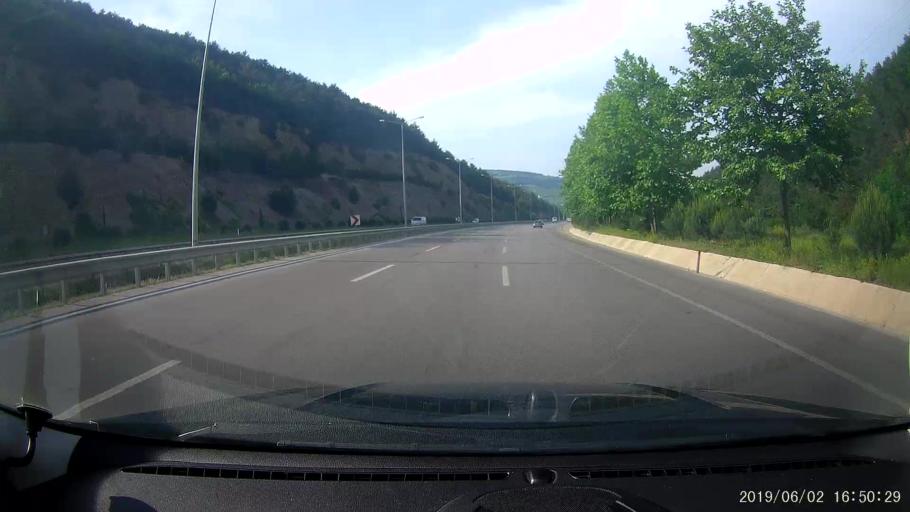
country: TR
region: Samsun
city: Samsun
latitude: 41.2556
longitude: 36.1737
